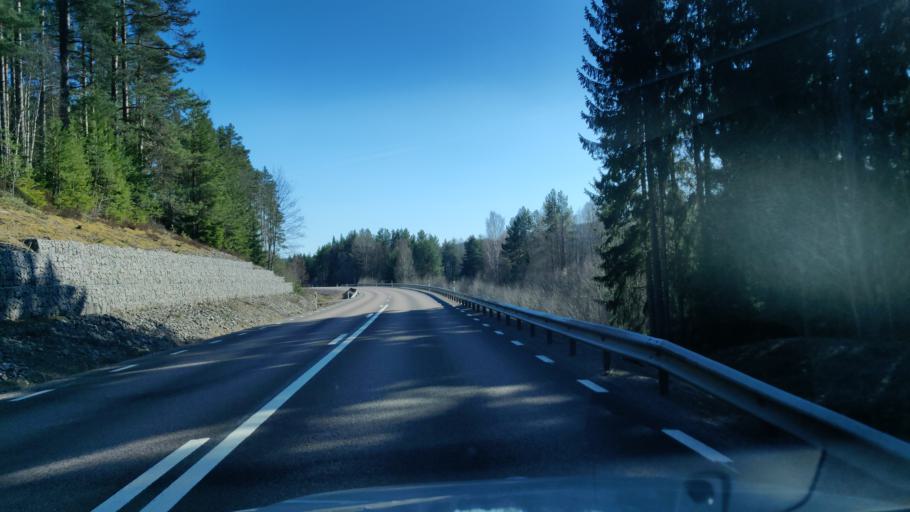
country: SE
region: Vaermland
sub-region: Hagfors Kommun
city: Hagfors
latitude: 59.9302
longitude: 13.6748
